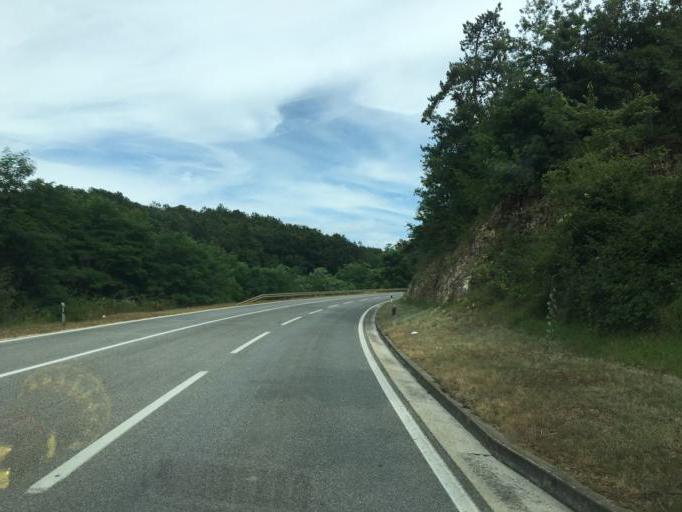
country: HR
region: Istarska
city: Pazin
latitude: 45.2396
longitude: 13.9137
